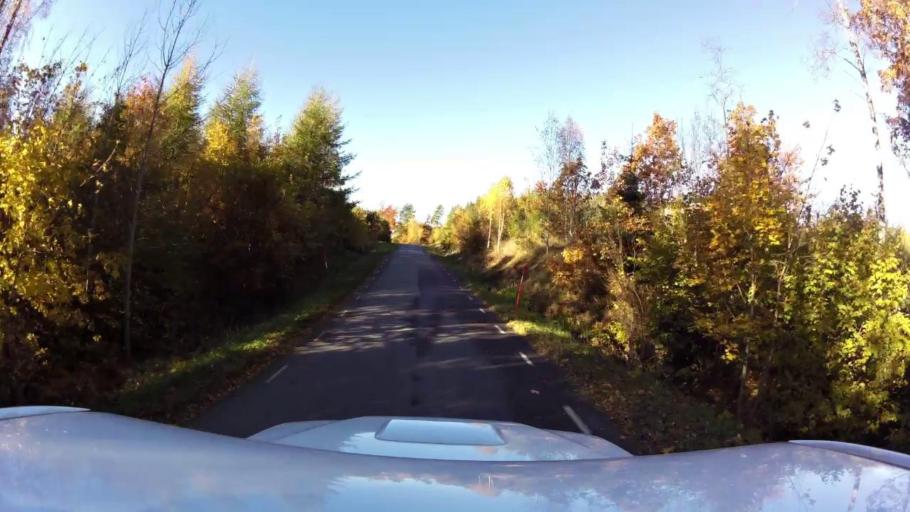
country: SE
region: OEstergoetland
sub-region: Linkopings Kommun
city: Ljungsbro
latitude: 58.5376
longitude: 15.4294
